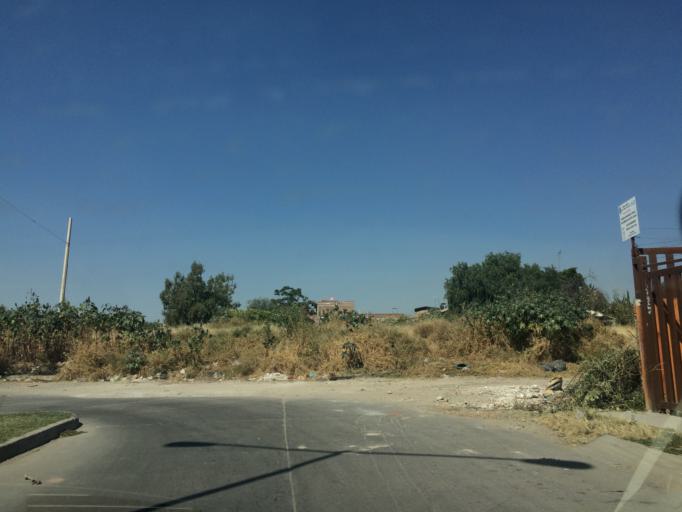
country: MX
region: Guanajuato
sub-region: Leon
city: San Jose de Duran (Los Troncoso)
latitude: 21.0932
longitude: -101.6694
